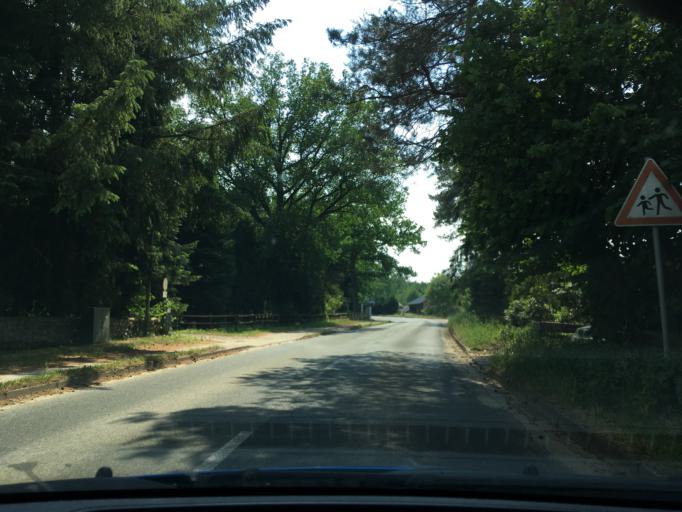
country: DE
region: Lower Saxony
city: Jesteburg
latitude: 53.2827
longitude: 9.9152
